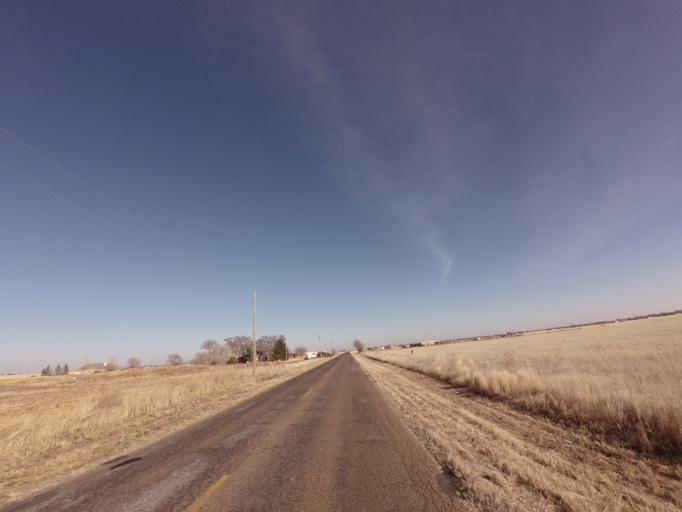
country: US
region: New Mexico
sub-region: Curry County
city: Clovis
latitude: 34.4192
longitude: -103.2469
